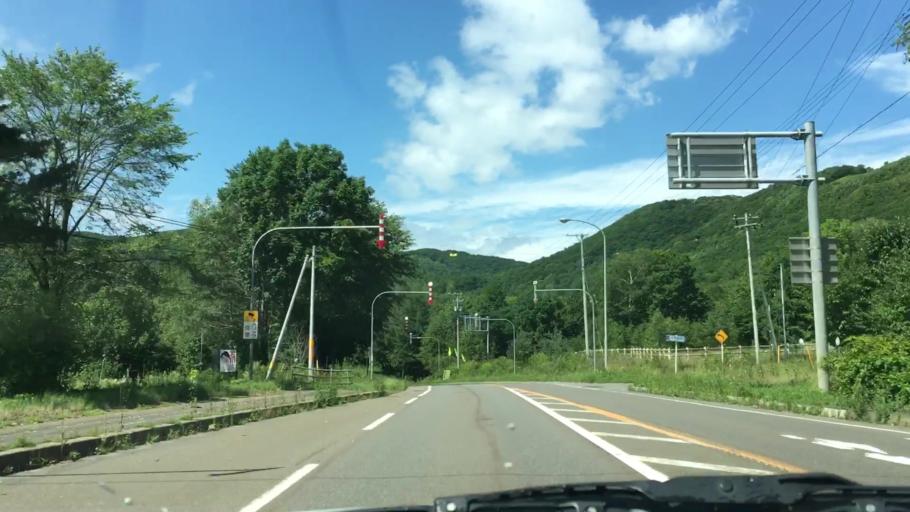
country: JP
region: Hokkaido
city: Otofuke
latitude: 43.2513
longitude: 143.4794
